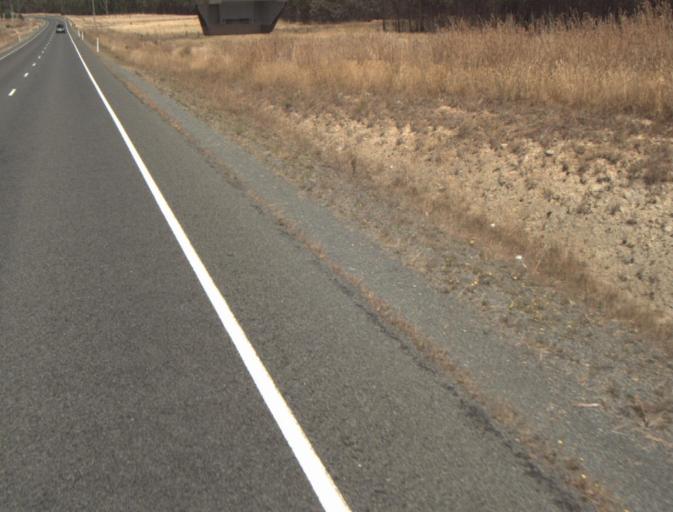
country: AU
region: Tasmania
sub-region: Launceston
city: Newstead
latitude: -41.3490
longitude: 147.3411
